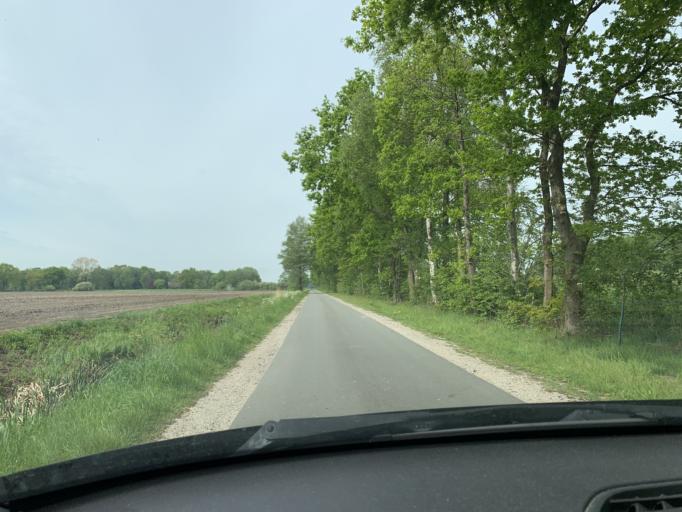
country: DE
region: Lower Saxony
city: Apen
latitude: 53.2119
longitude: 7.7821
